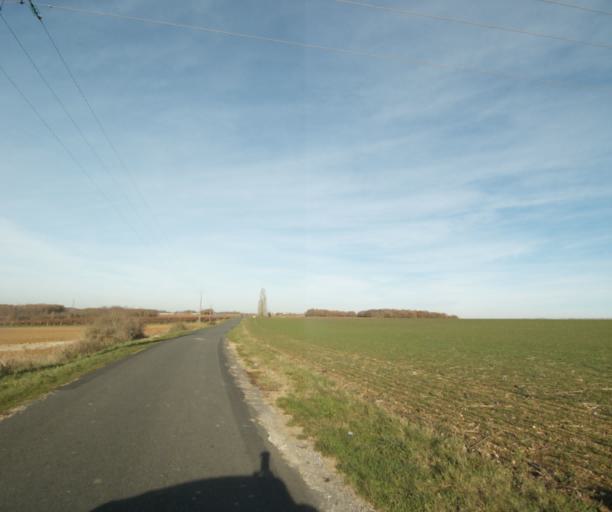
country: FR
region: Poitou-Charentes
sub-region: Departement de la Charente-Maritime
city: Chaniers
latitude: 45.7218
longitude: -0.5288
